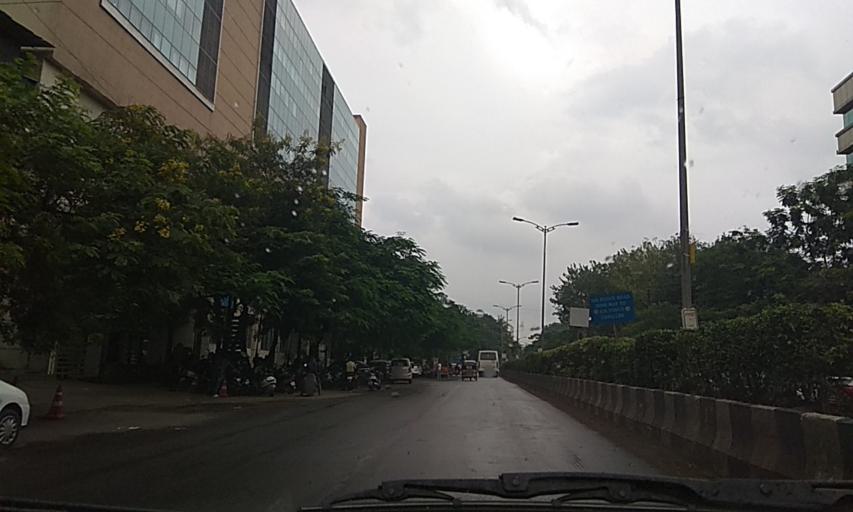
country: IN
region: Maharashtra
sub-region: Pune Division
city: Lohogaon
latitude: 18.5625
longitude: 73.9181
